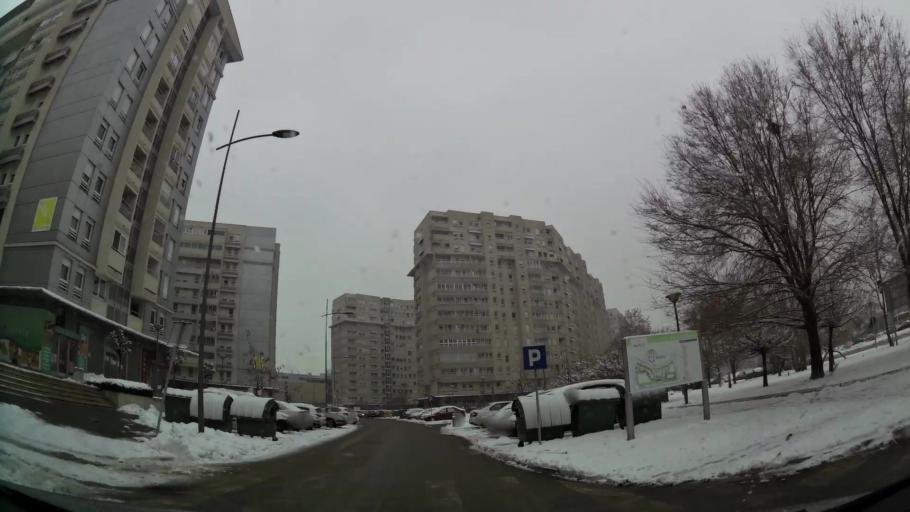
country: RS
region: Central Serbia
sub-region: Belgrade
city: Novi Beograd
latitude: 44.8060
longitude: 20.4087
